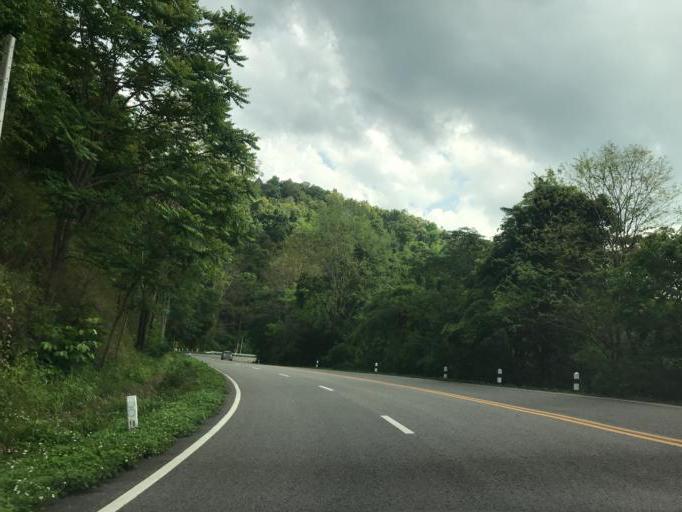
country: TH
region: Phayao
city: Phayao
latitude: 19.0697
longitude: 99.8107
